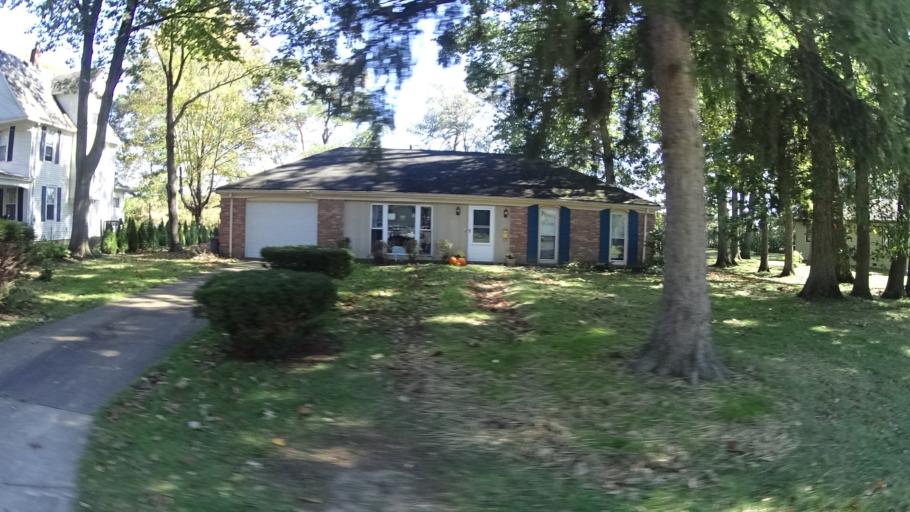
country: US
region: Ohio
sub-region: Lorain County
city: Oberlin
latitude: 41.2973
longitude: -82.2264
